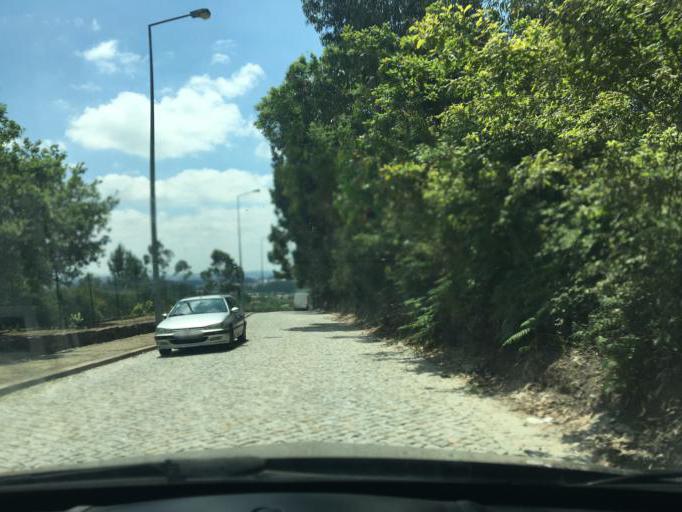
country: PT
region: Porto
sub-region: Maia
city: Anta
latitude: 41.2898
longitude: -8.6145
